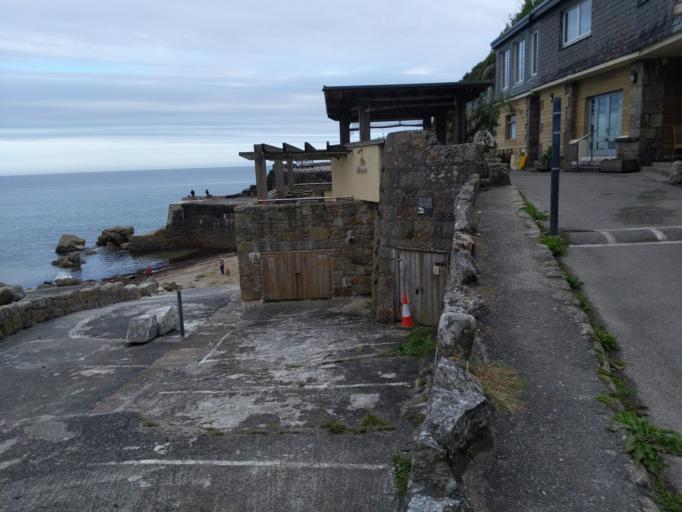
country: GB
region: England
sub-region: Cornwall
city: St. Buryan
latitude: 50.0621
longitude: -5.5647
